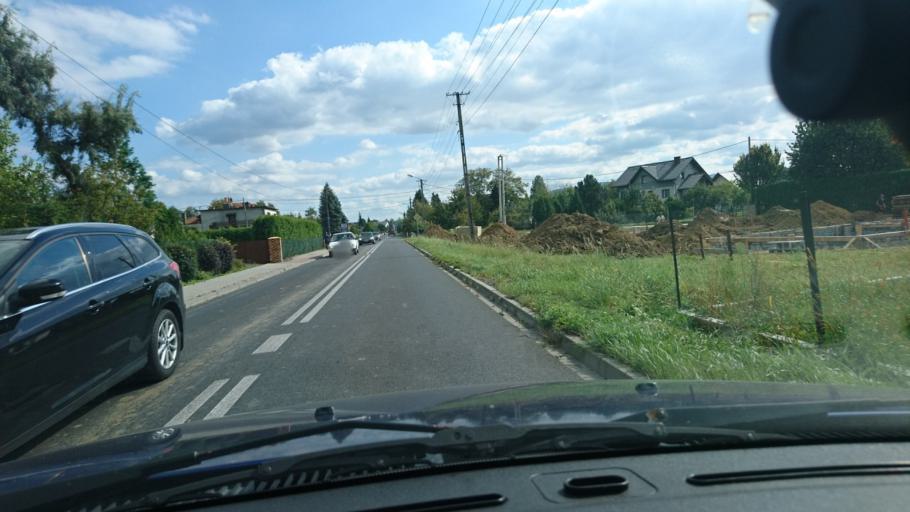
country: PL
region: Silesian Voivodeship
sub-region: Powiat bielski
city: Mazancowice
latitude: 49.8652
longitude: 18.9704
